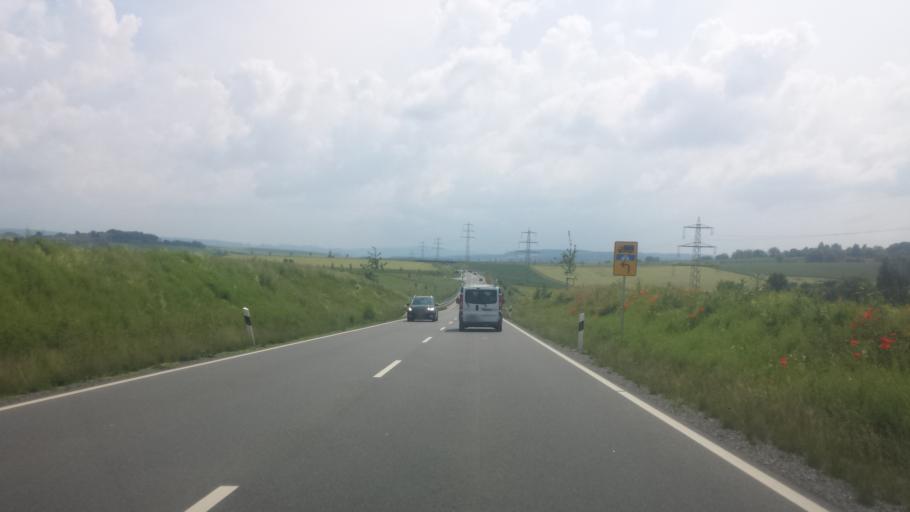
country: DE
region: Hesse
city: Reinheim
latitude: 49.8240
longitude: 8.8152
